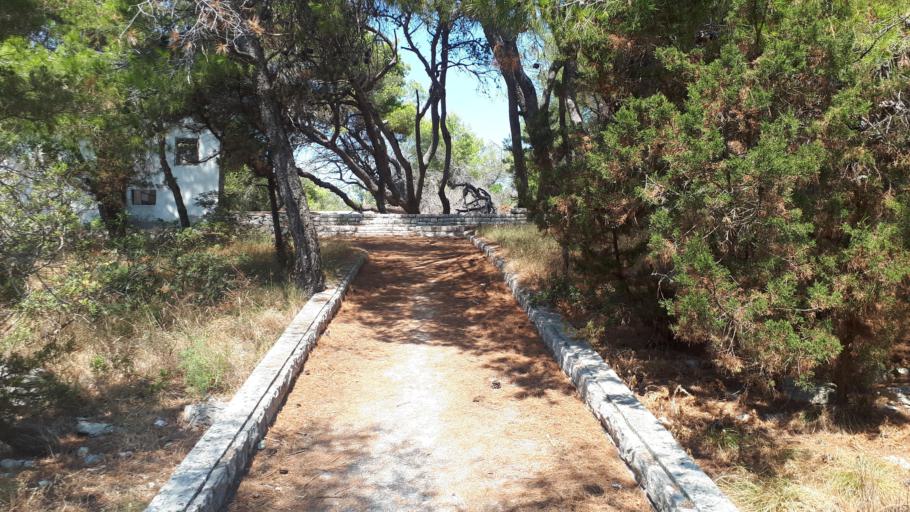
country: HR
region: Splitsko-Dalmatinska
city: Jelsa
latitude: 43.1902
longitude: 16.6929
